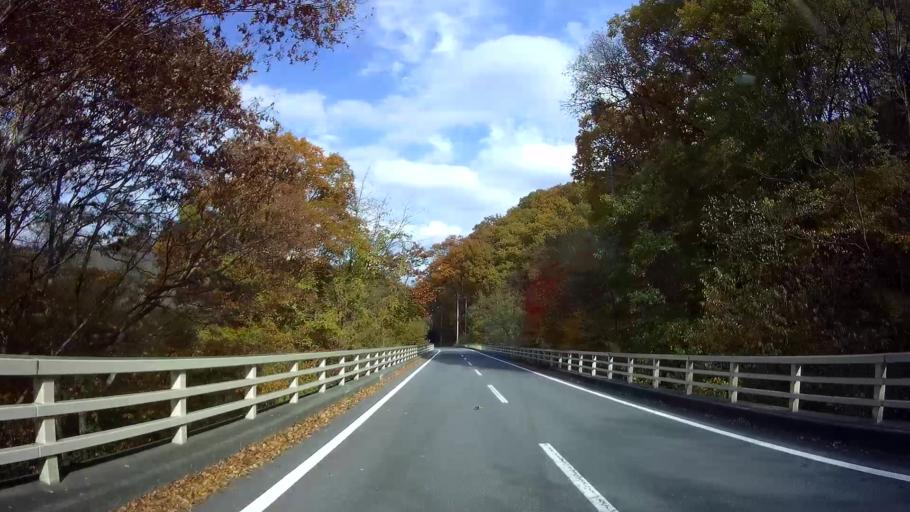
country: JP
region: Gunma
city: Nakanojomachi
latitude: 36.5310
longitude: 138.6578
